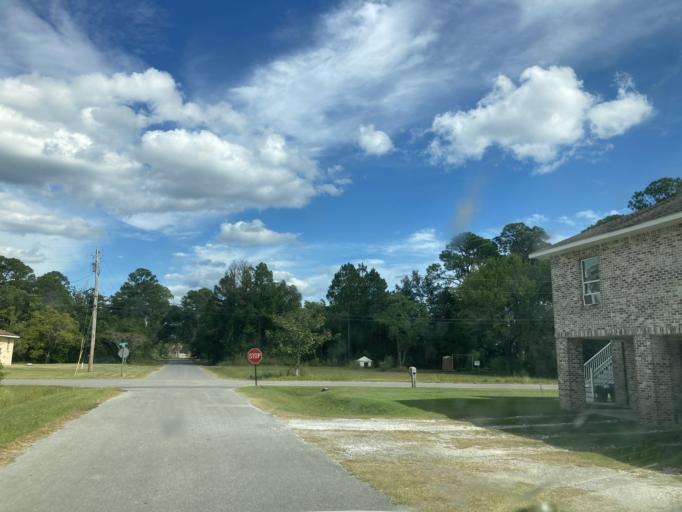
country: US
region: Mississippi
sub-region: Jackson County
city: Saint Martin
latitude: 30.4394
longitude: -88.8742
